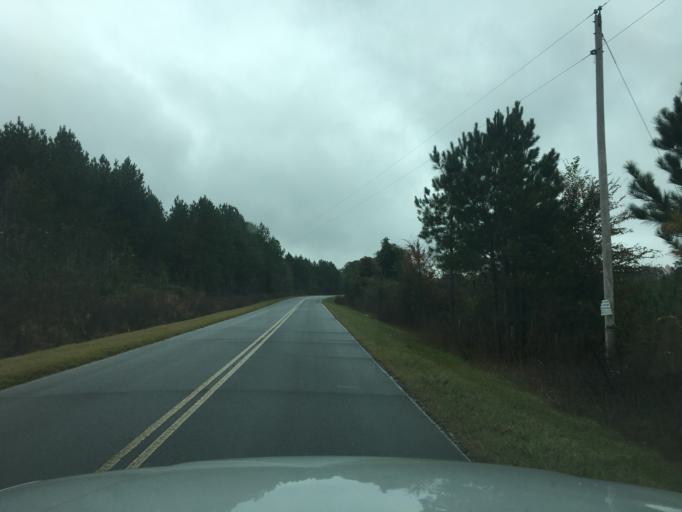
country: US
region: South Carolina
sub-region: Pickens County
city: Central
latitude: 34.7468
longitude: -82.7729
